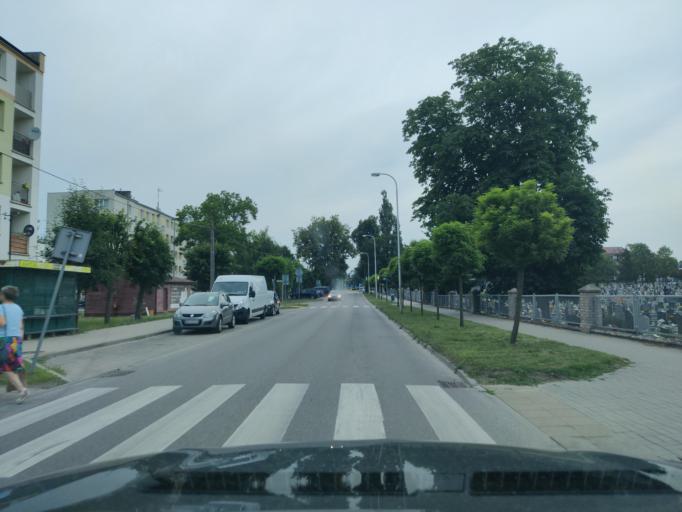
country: PL
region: Warmian-Masurian Voivodeship
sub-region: Powiat dzialdowski
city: Dzialdowo
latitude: 53.2402
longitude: 20.1870
